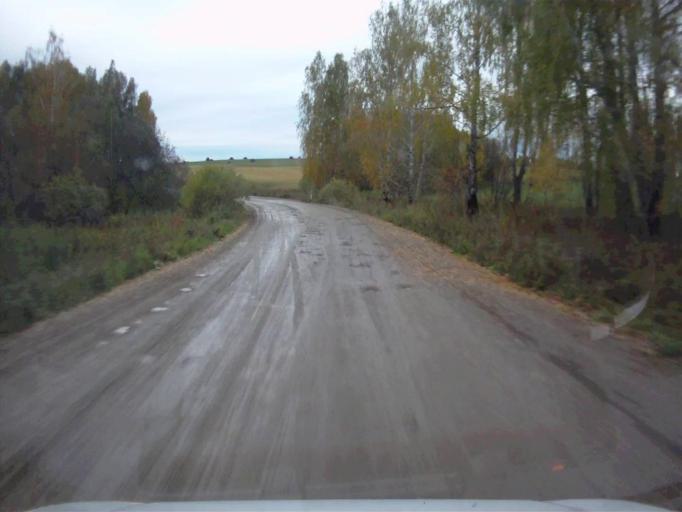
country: RU
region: Sverdlovsk
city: Mikhaylovsk
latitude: 56.1754
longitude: 59.2155
